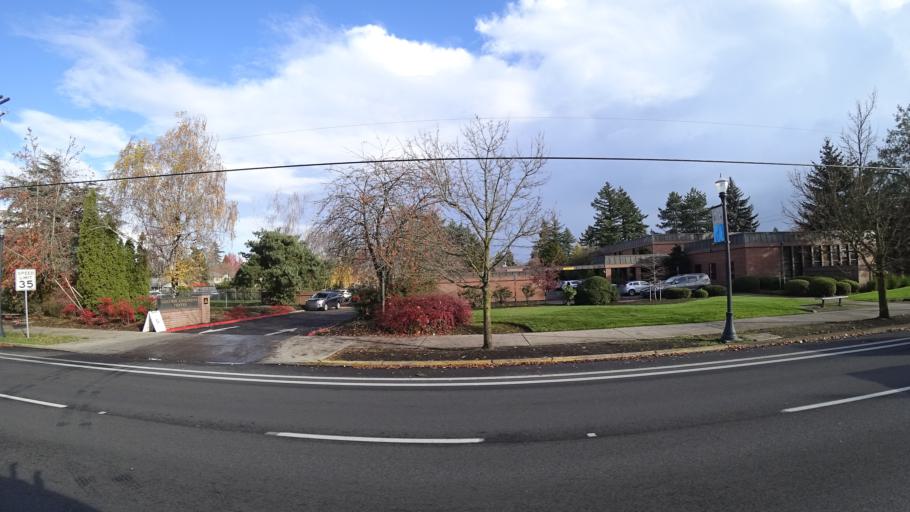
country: US
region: Oregon
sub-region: Multnomah County
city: Lents
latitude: 45.5233
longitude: -122.5583
